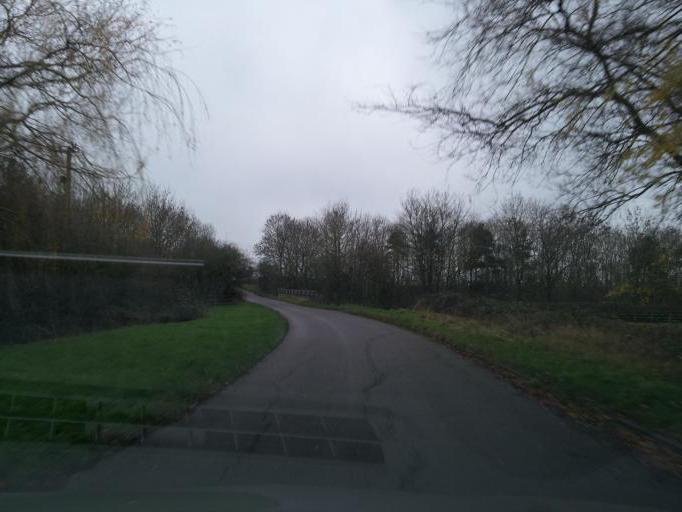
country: GB
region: England
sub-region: Warwickshire
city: Rugby
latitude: 52.3366
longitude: -1.1979
